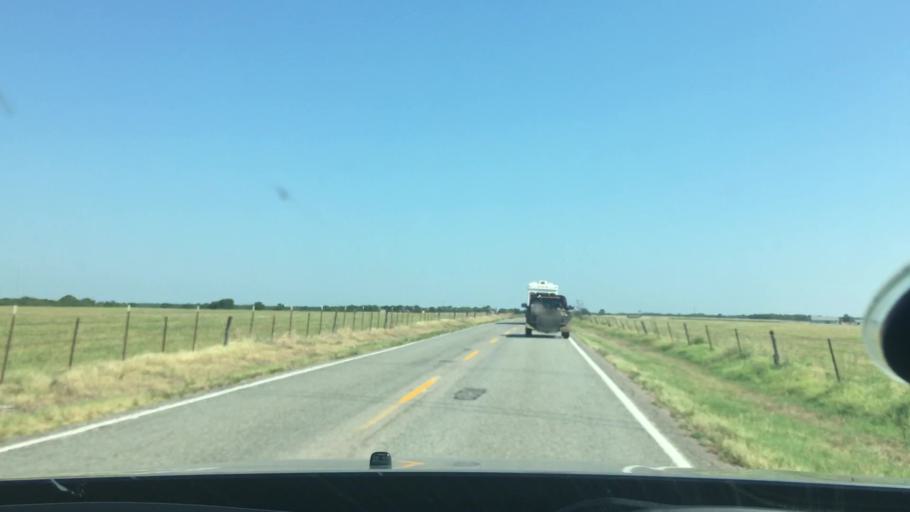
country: US
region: Oklahoma
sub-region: Johnston County
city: Tishomingo
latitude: 34.1665
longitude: -96.5089
